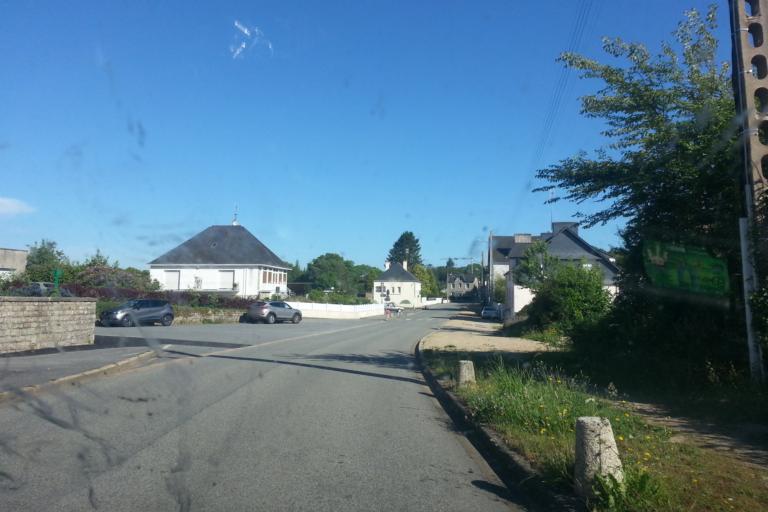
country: FR
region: Brittany
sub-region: Departement du Morbihan
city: Le Faouet
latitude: 48.0365
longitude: -3.4954
